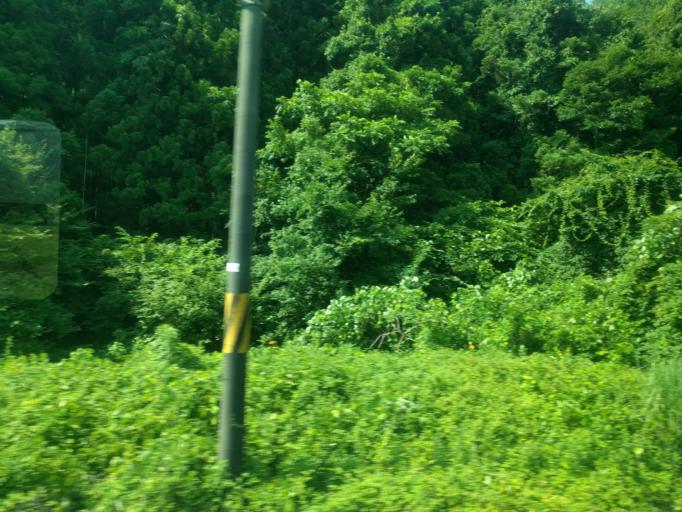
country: JP
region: Fukushima
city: Inawashiro
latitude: 37.4806
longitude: 140.1842
